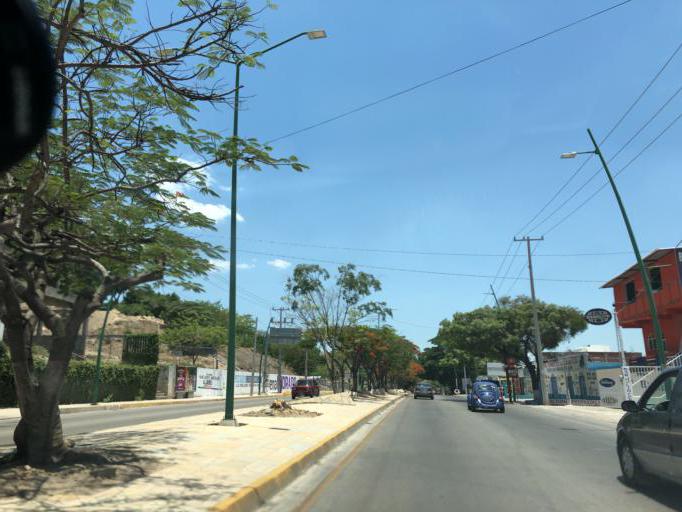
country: MX
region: Chiapas
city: Tuxtla Gutierrez
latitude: 16.7455
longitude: -93.1354
